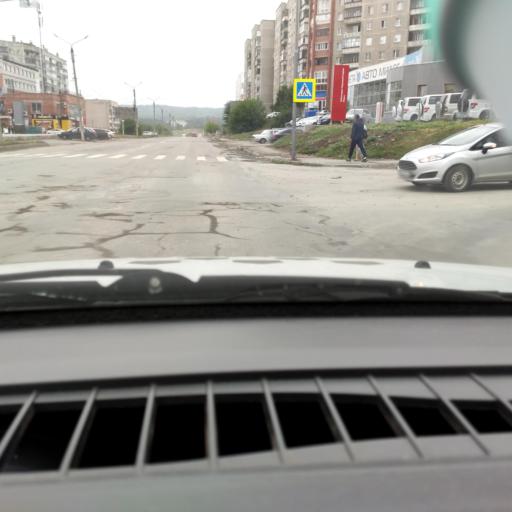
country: RU
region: Chelyabinsk
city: Miass
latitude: 55.0455
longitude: 60.0988
